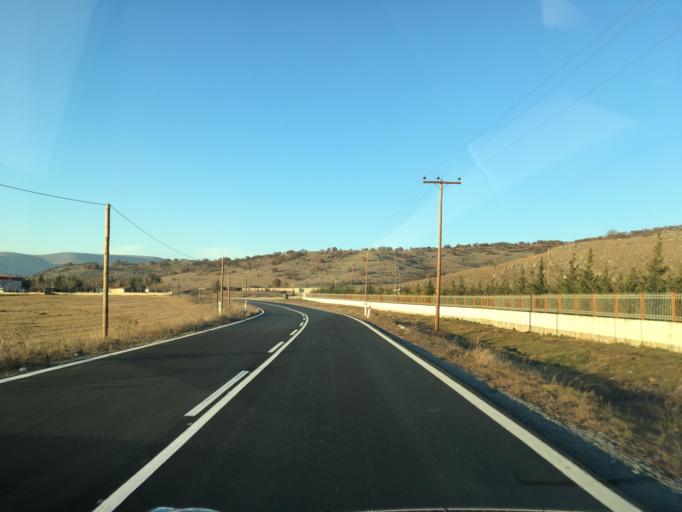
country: GR
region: West Macedonia
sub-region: Nomos Kozanis
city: Kozani
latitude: 40.3021
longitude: 21.7361
